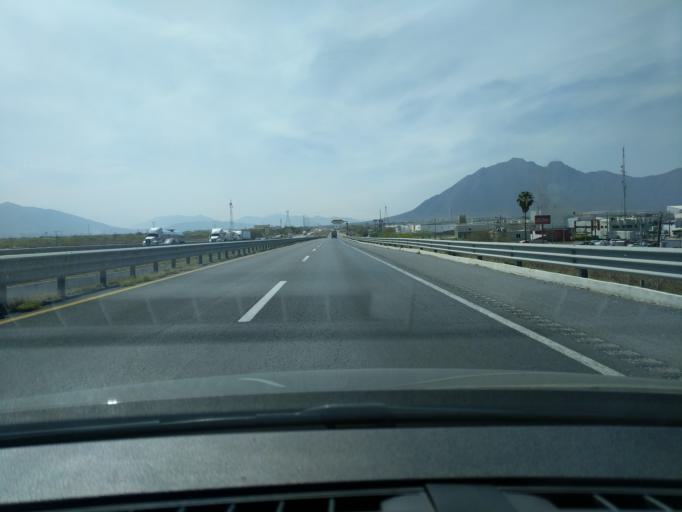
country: MX
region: Nuevo Leon
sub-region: General Escobedo
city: Union Agropecuarios Lazaro Cardenas del Norte
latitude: 25.8239
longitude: -100.3601
